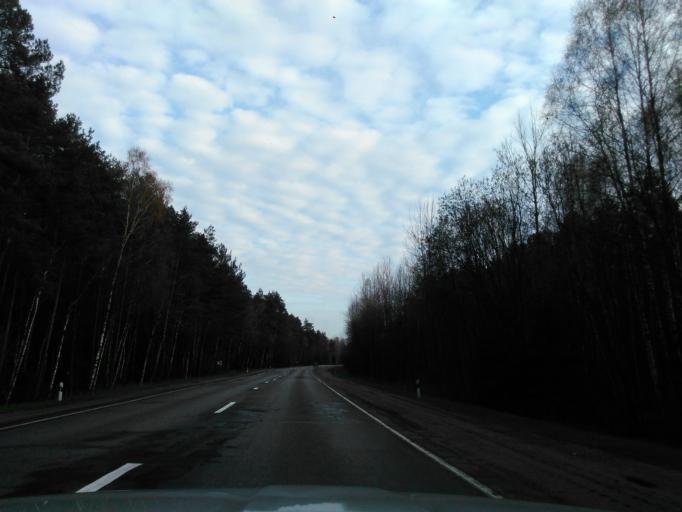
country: BY
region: Minsk
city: Plyeshchanitsy
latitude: 54.3747
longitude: 27.8815
